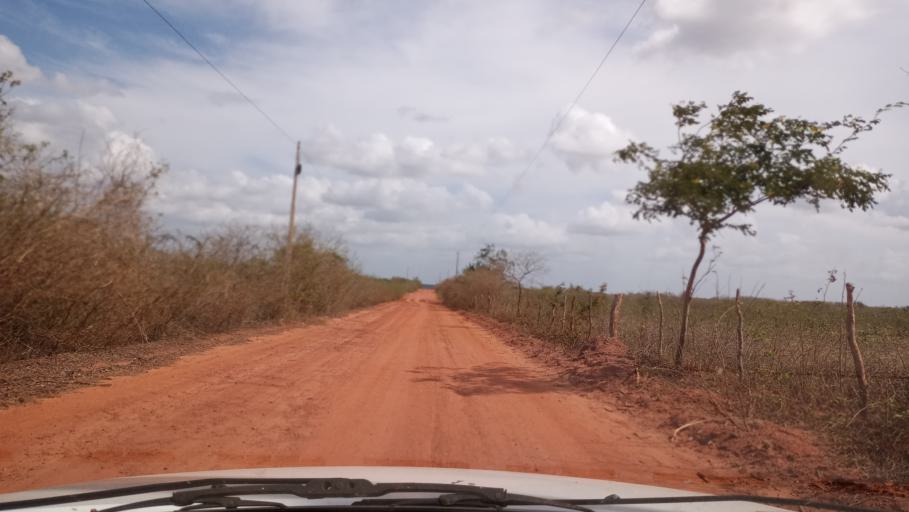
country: BR
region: Rio Grande do Norte
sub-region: Joao Camara
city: Joao Camara
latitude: -5.4574
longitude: -35.8382
